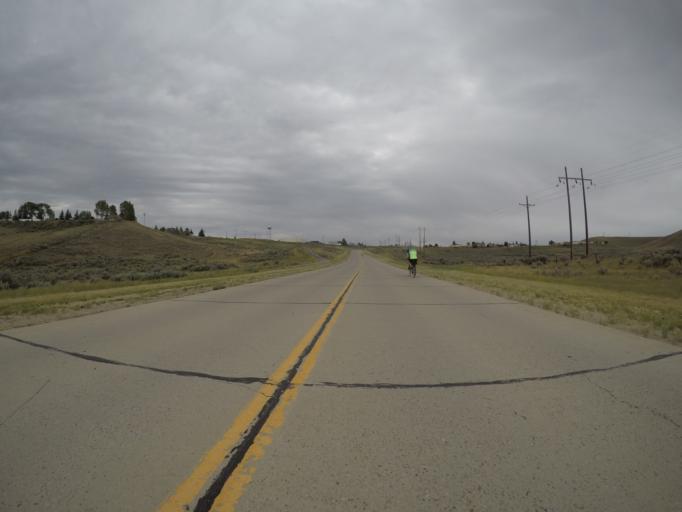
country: US
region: Wyoming
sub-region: Lincoln County
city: Kemmerer
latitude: 41.7961
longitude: -110.5476
